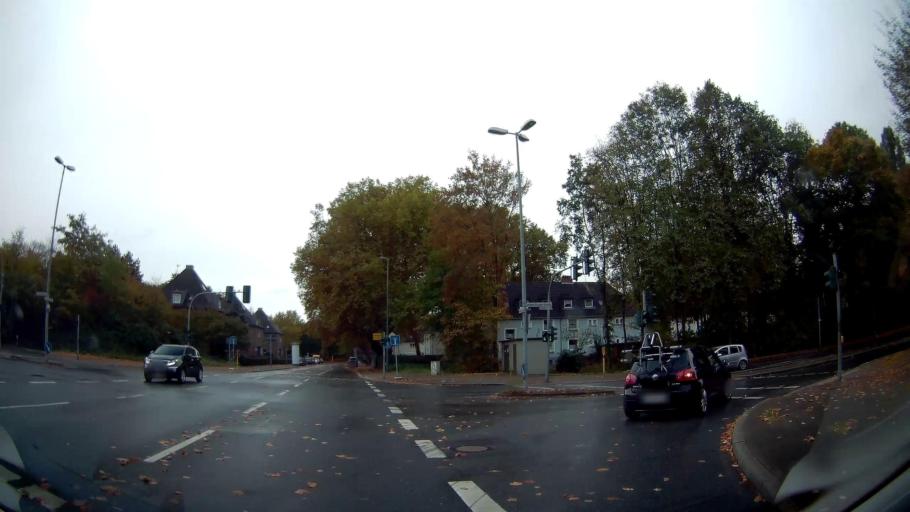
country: DE
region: North Rhine-Westphalia
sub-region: Regierungsbezirk Munster
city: Gelsenkirchen
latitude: 51.5402
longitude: 7.0860
